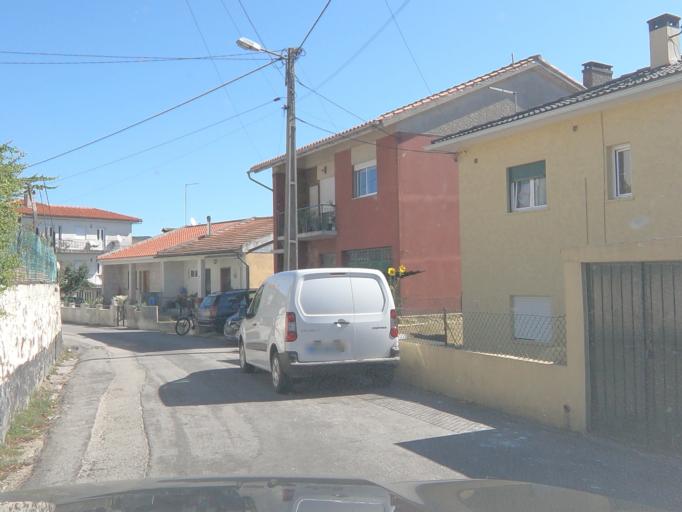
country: PT
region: Vila Real
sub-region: Vila Real
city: Vila Real
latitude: 41.3169
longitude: -7.7296
